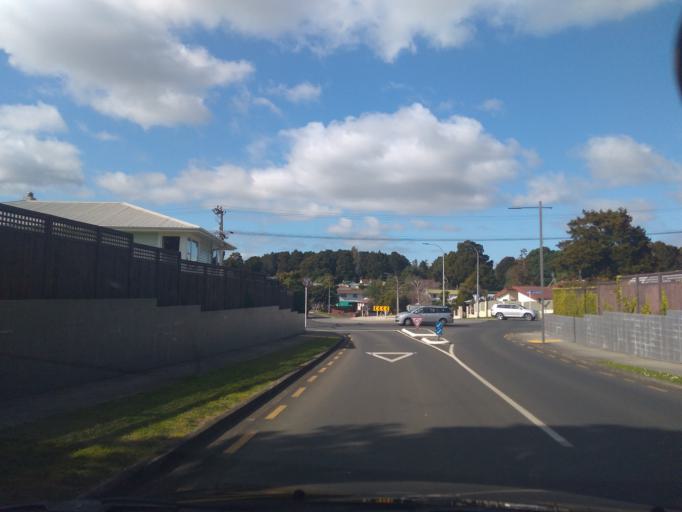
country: NZ
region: Northland
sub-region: Whangarei
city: Whangarei
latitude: -35.6795
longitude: 174.3171
